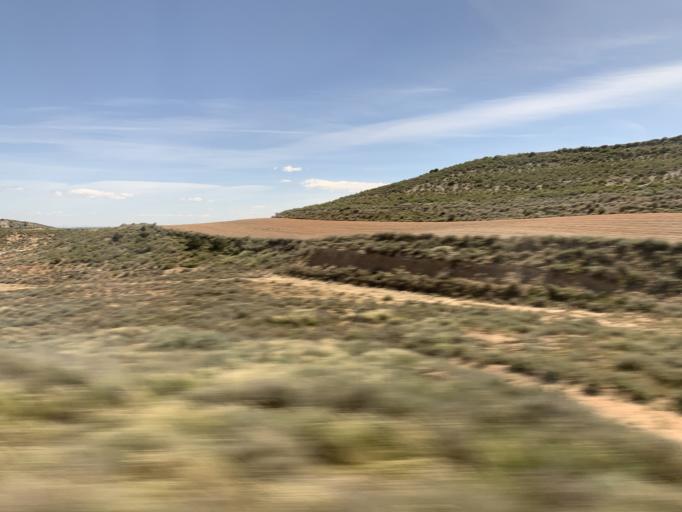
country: ES
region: Aragon
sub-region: Provincia de Huesca
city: Penalba
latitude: 41.5265
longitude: -0.0298
